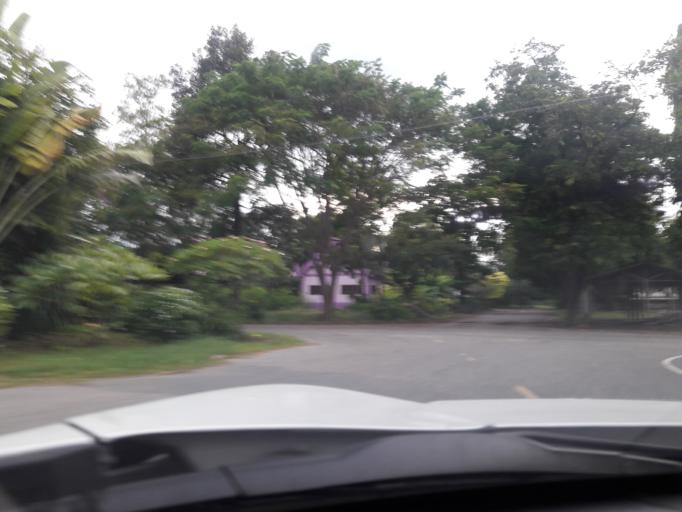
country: TH
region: Lop Buri
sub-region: Amphoe Tha Luang
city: Tha Luang
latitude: 15.0679
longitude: 101.1068
